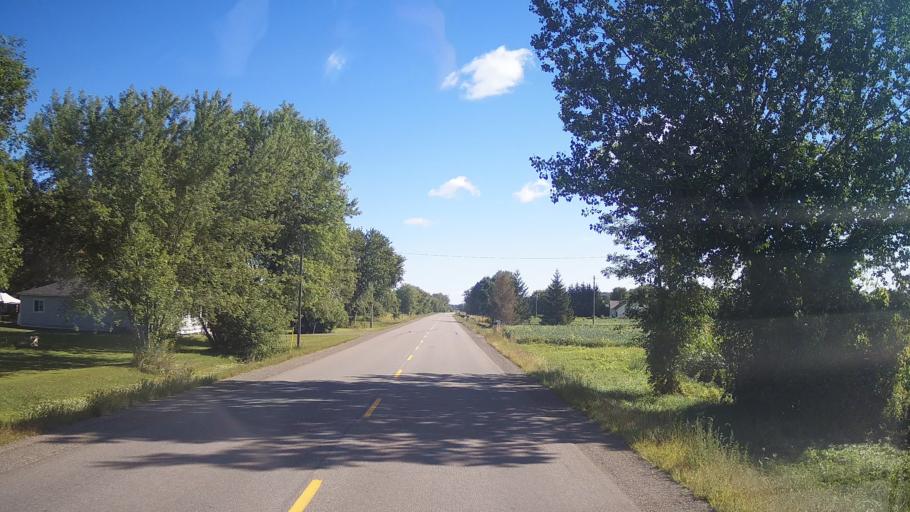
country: CA
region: Ontario
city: Prescott
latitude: 44.8989
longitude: -75.4545
